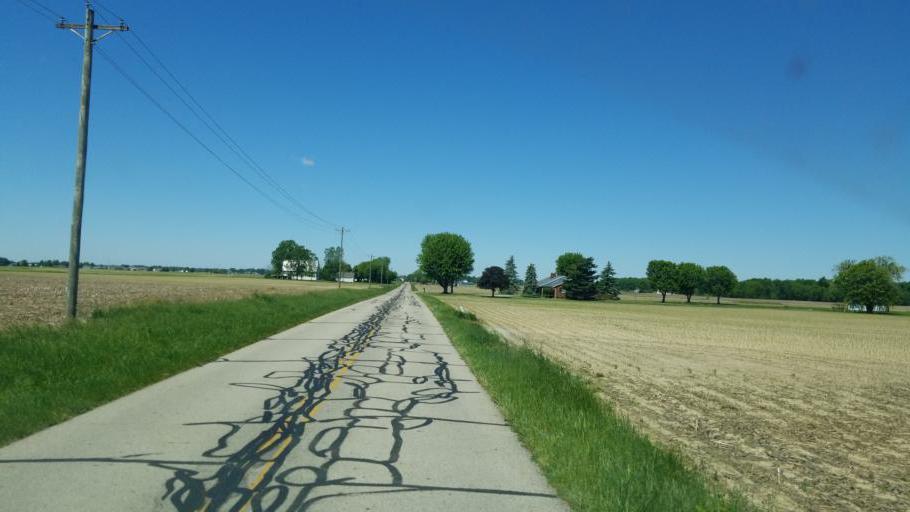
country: US
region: Ohio
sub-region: Shelby County
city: Anna
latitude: 40.3804
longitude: -84.2241
